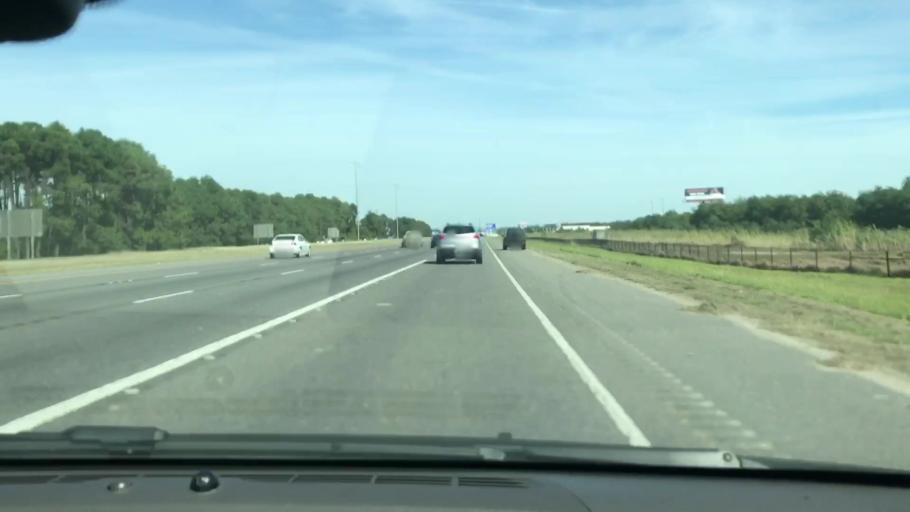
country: US
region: Louisiana
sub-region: Saint Tammany Parish
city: Eden Isle
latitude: 30.2262
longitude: -89.7785
